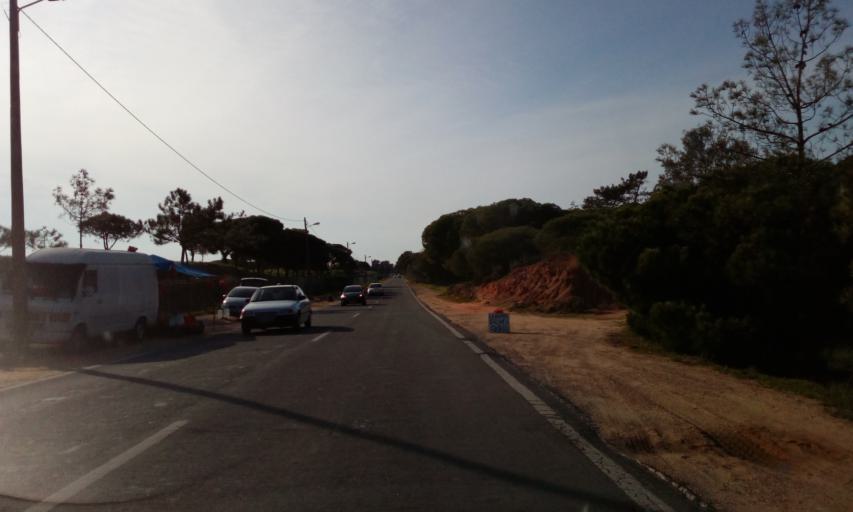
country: PT
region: Faro
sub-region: Faro
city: Faro
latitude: 37.0216
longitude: -7.9785
